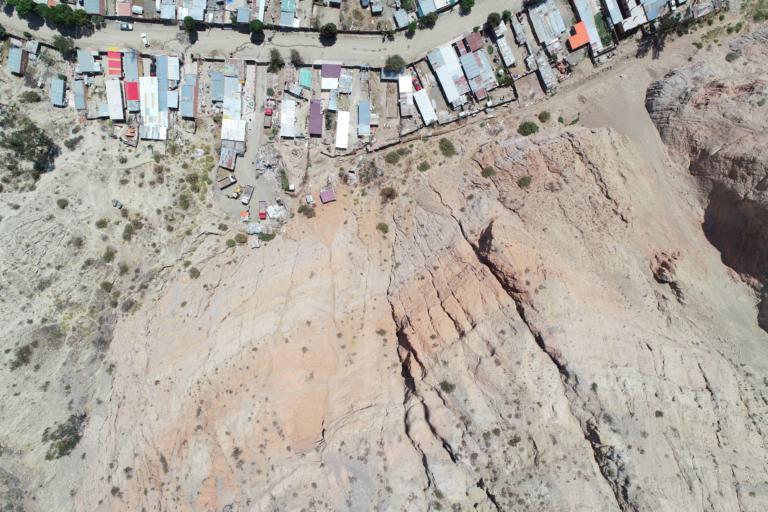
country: BO
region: La Paz
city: La Paz
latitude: -16.5284
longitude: -68.0905
